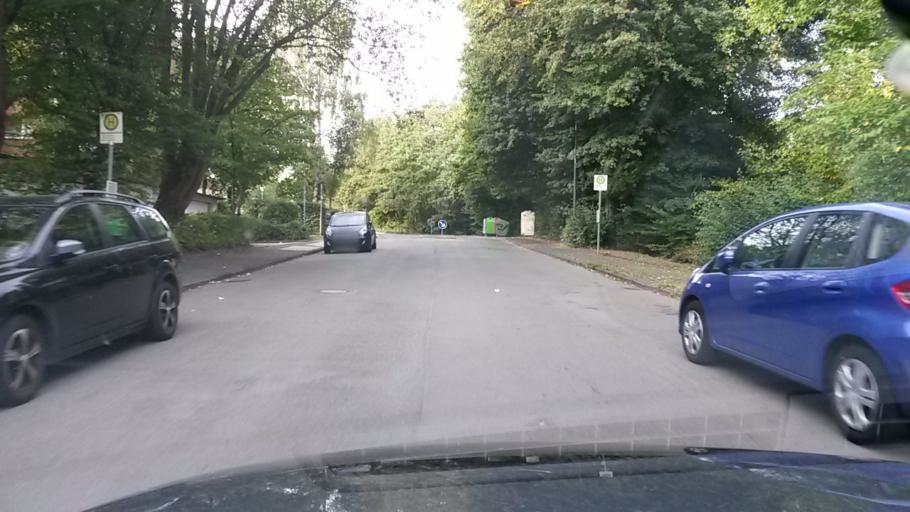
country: DE
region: North Rhine-Westphalia
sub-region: Regierungsbezirk Arnsberg
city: Luedenscheid
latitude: 51.2301
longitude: 7.6402
